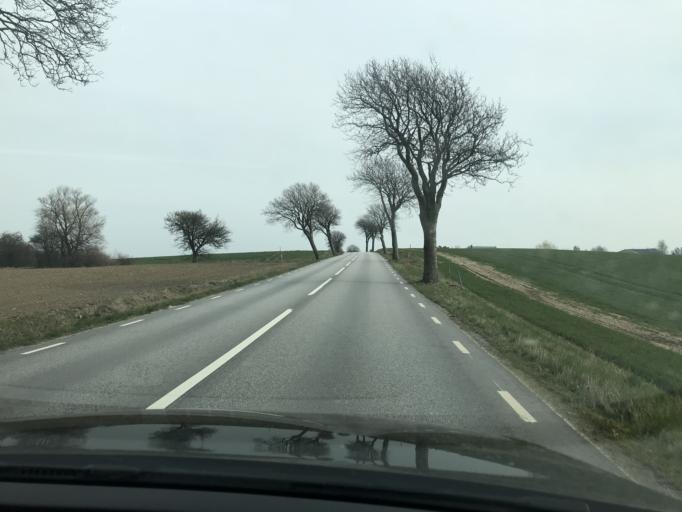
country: SE
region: Skane
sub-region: Skurups Kommun
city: Skivarp
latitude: 55.4219
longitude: 13.6243
